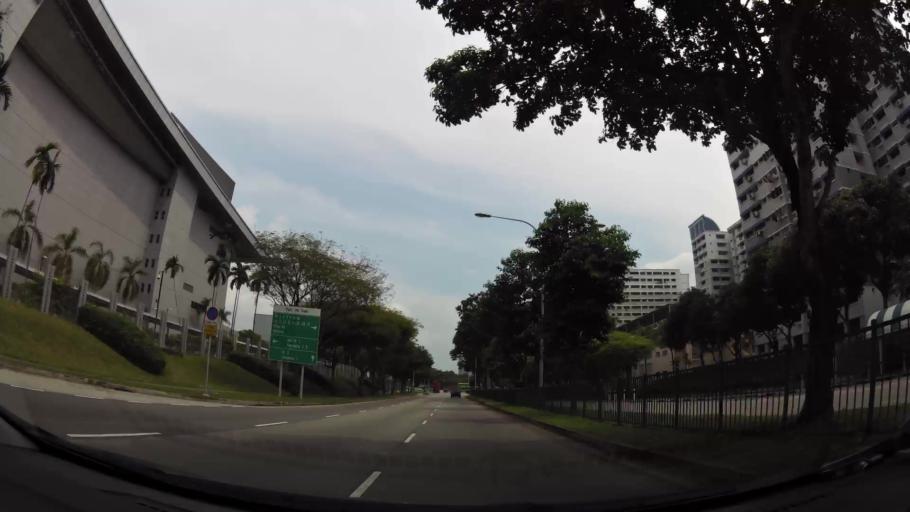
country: MY
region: Johor
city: Kampung Pasir Gudang Baru
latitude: 1.3783
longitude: 103.9332
